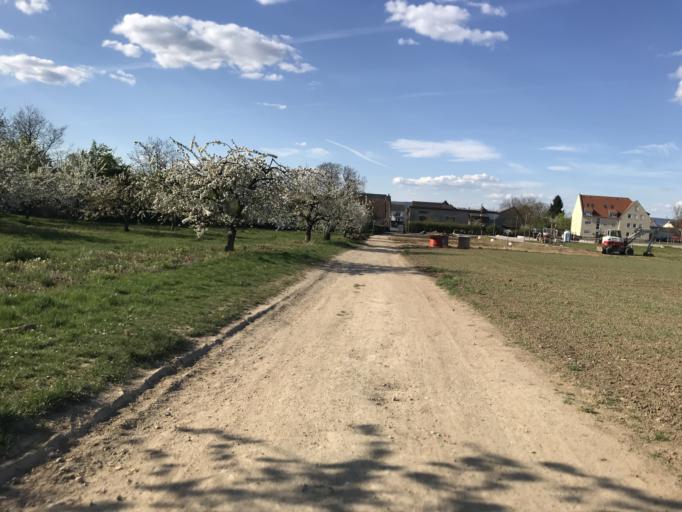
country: DE
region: Rheinland-Pfalz
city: Wackernheim
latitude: 49.9728
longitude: 8.1199
